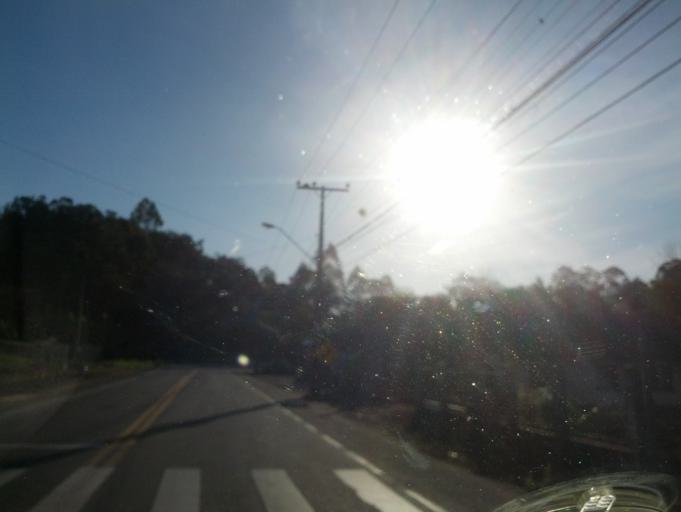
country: BR
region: Santa Catarina
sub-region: Indaial
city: Indaial
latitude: -26.8836
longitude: -49.1745
